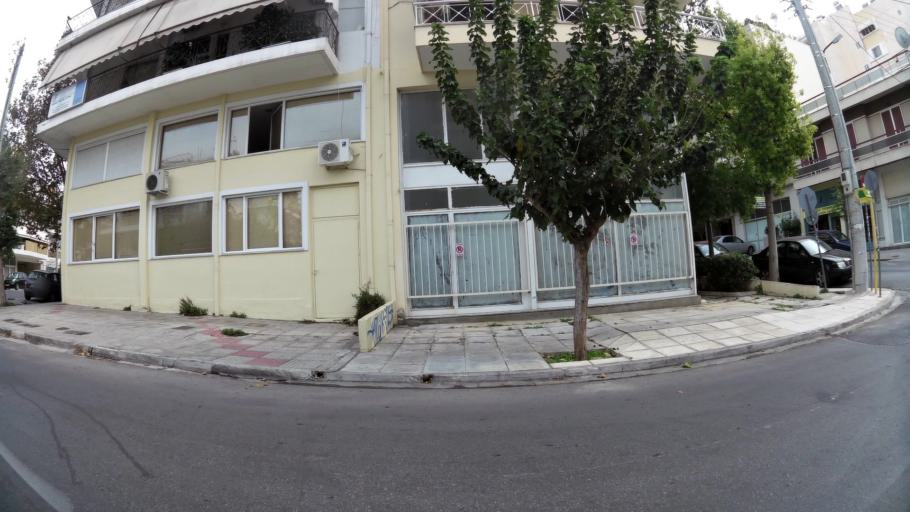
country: GR
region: Attica
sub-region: Nomarchia Athinas
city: Alimos
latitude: 37.9209
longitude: 23.7291
